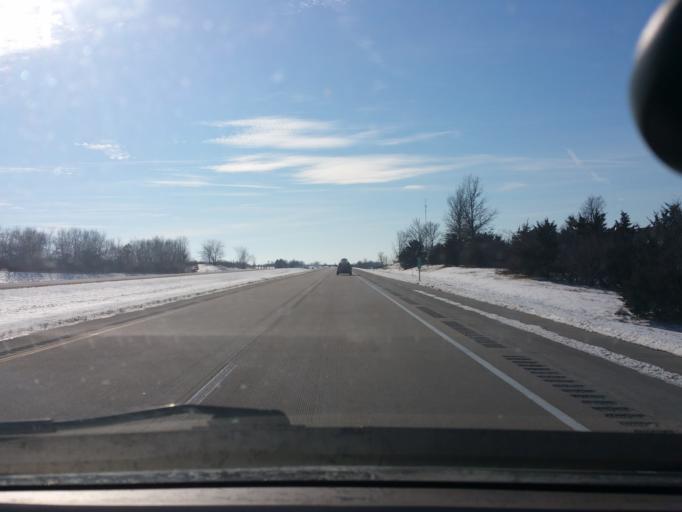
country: US
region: Iowa
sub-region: Decatur County
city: Leon
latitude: 40.7708
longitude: -93.8363
